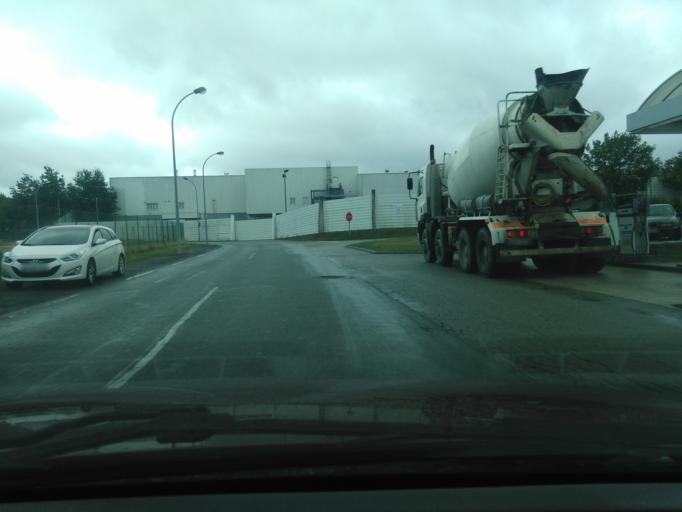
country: FR
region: Pays de la Loire
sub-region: Departement de la Vendee
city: La Roche-sur-Yon
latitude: 46.6730
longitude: -1.4045
